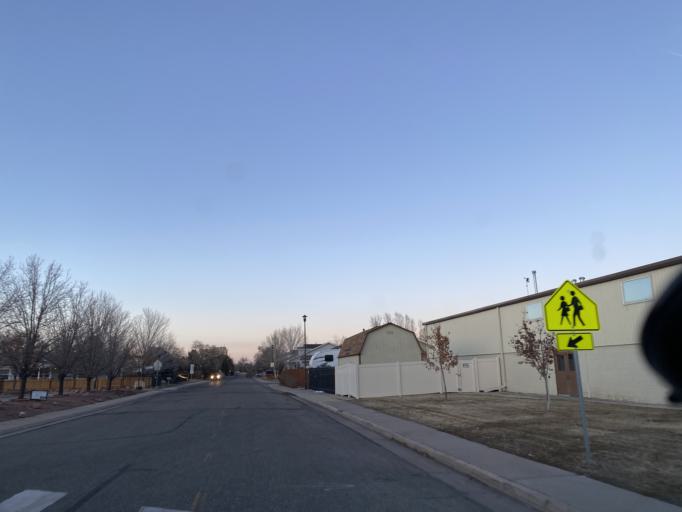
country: US
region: Colorado
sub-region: Adams County
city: Brighton
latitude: 39.9737
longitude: -104.8167
